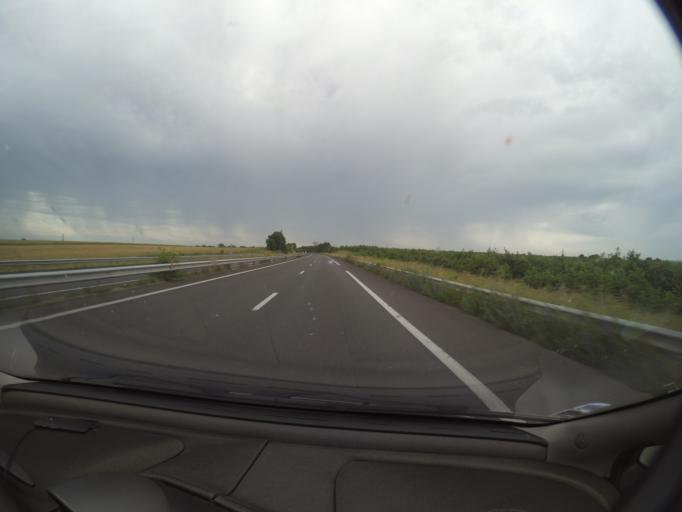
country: FR
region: Pays de la Loire
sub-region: Departement de la Sarthe
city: Noyen-sur-Sarthe
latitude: 47.8770
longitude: -0.1172
